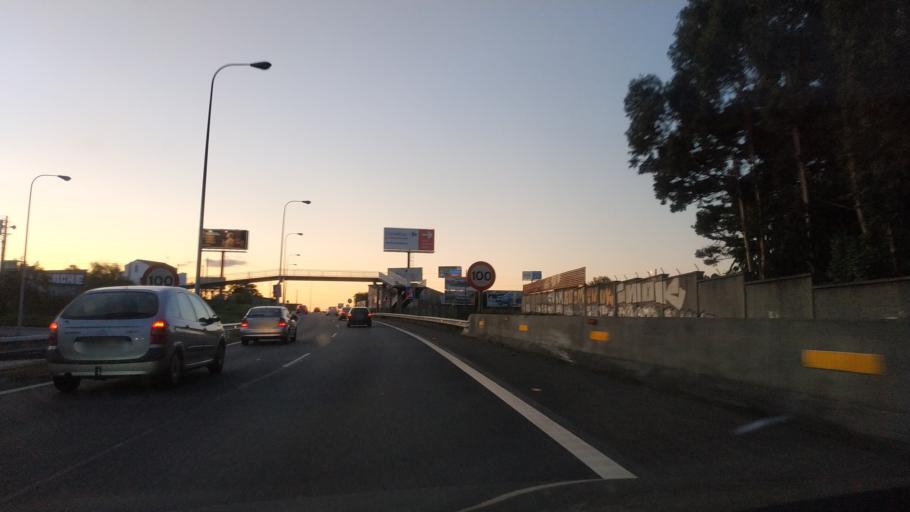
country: ES
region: Galicia
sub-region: Provincia da Coruna
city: A Coruna
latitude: 43.3316
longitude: -8.3986
